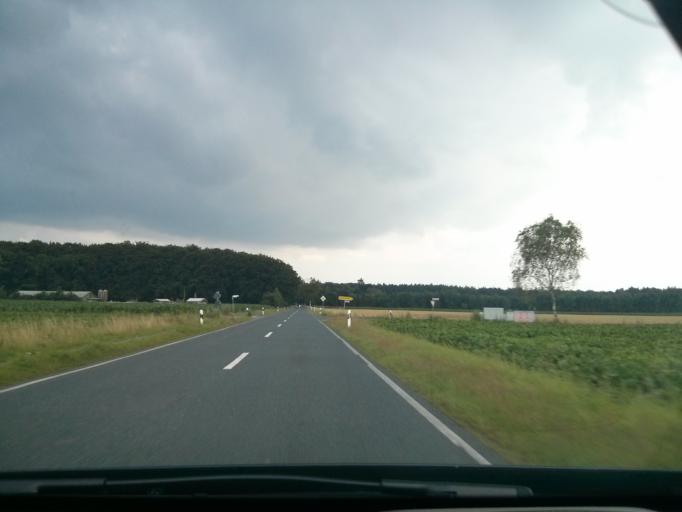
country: DE
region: Lower Saxony
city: Bendestorf
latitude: 53.3568
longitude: 9.9412
